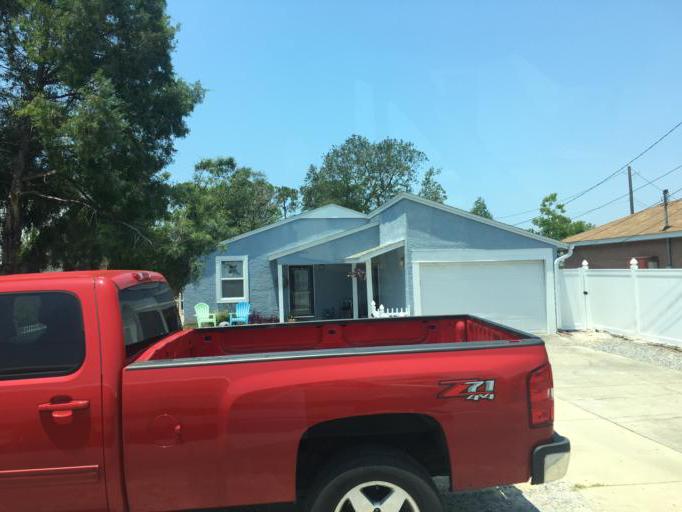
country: US
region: Florida
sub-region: Bay County
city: Panama City Beach
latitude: 30.2089
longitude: -85.8546
